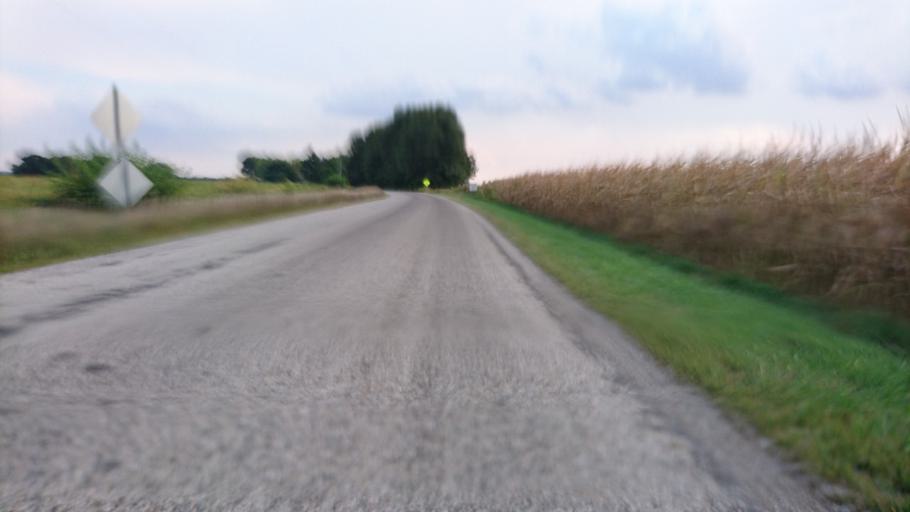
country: US
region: Illinois
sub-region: Logan County
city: Atlanta
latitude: 40.2315
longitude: -89.2048
